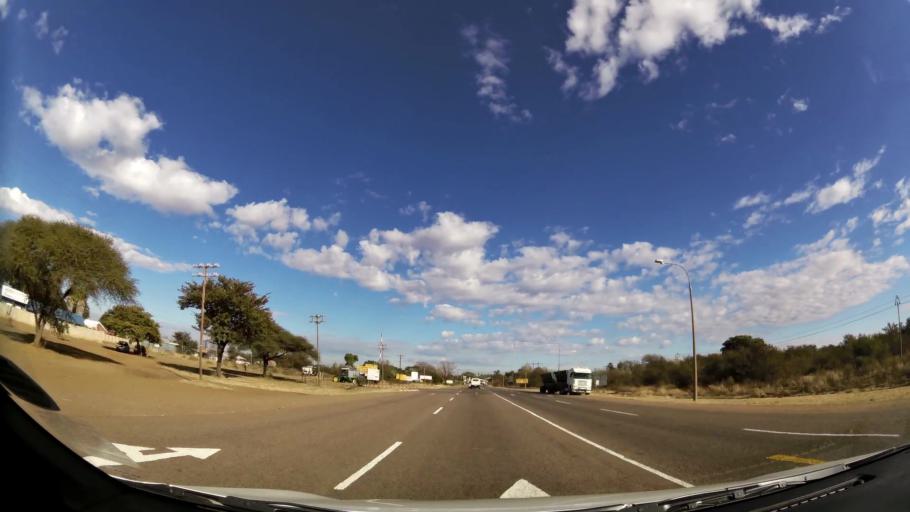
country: ZA
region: Limpopo
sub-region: Waterberg District Municipality
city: Bela-Bela
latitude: -24.8915
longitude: 28.3020
